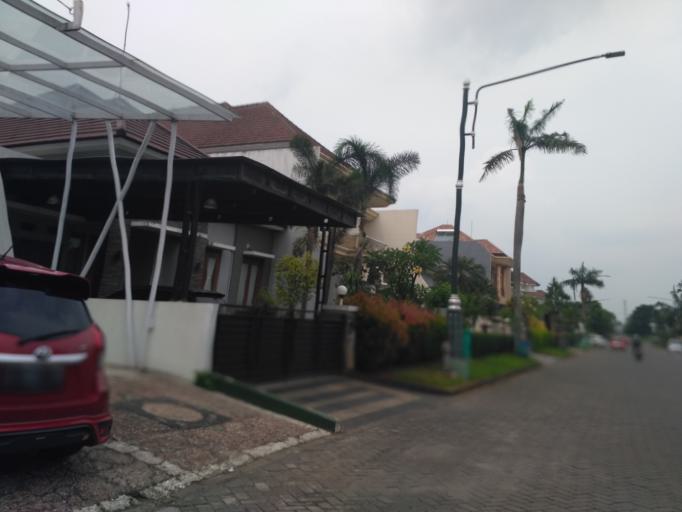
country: ID
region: Central Java
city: Semarang
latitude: -7.0607
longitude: 110.4301
